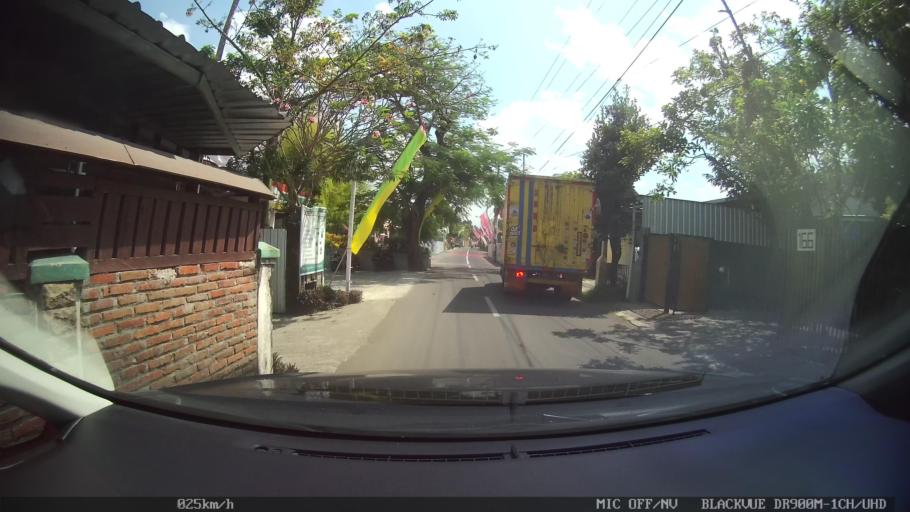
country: ID
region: Daerah Istimewa Yogyakarta
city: Yogyakarta
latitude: -7.8294
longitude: 110.3878
